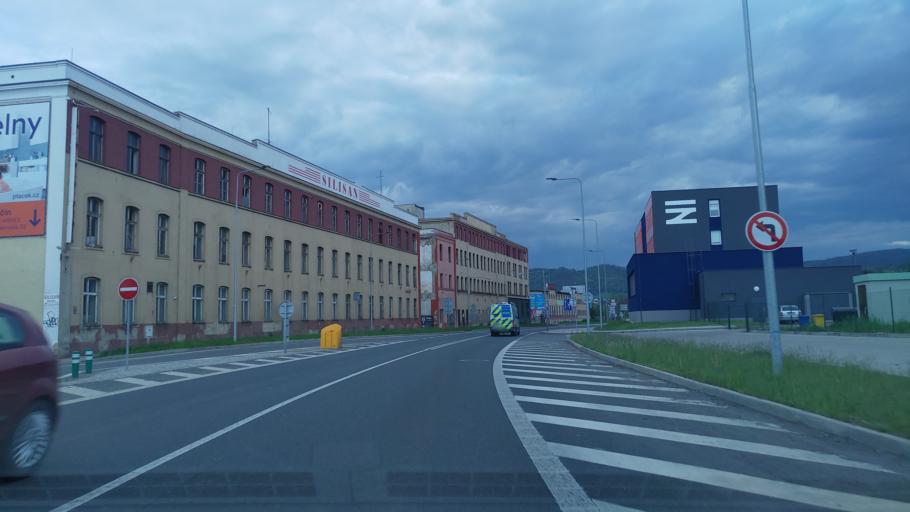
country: CZ
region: Ustecky
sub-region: Okres Decin
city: Decin
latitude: 50.7609
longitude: 14.1979
